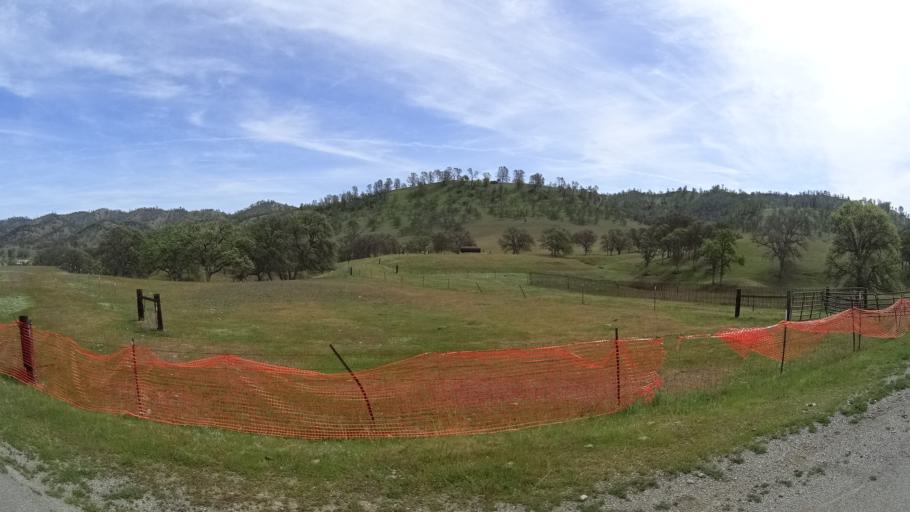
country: US
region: California
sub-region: Glenn County
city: Willows
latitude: 39.6095
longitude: -122.5260
